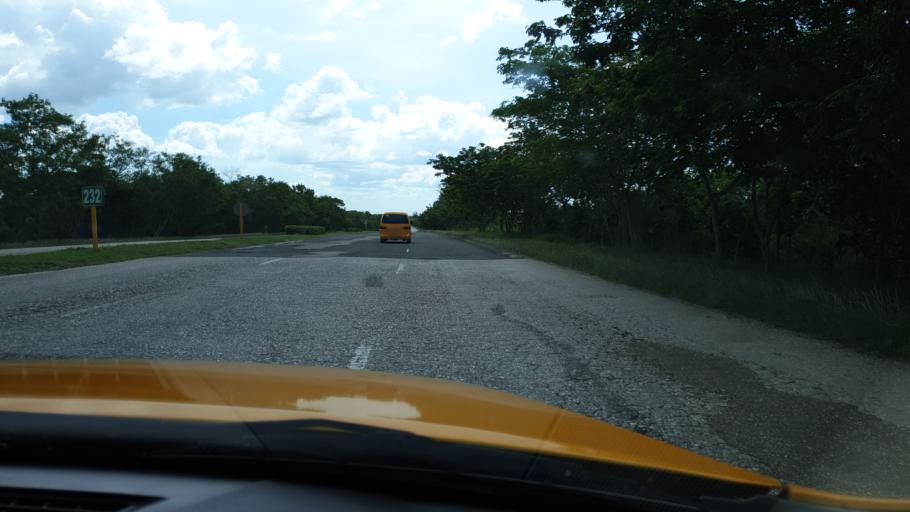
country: CU
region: Cienfuegos
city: Cruces
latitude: 22.4537
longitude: -80.2950
